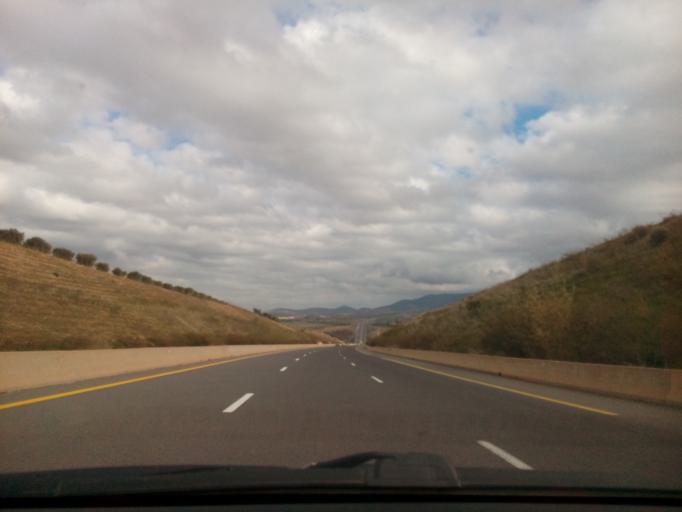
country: DZ
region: Tlemcen
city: Chetouane
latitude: 34.9776
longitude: -1.2539
